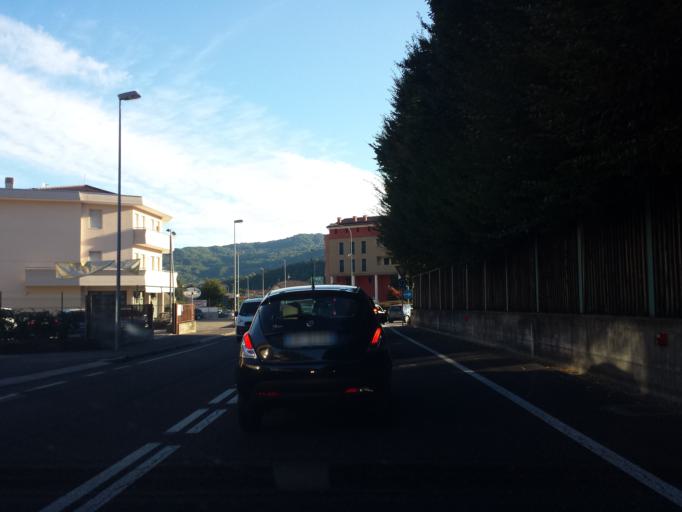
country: IT
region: Veneto
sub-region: Provincia di Vicenza
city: Valdagno
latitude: 45.6382
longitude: 11.3079
